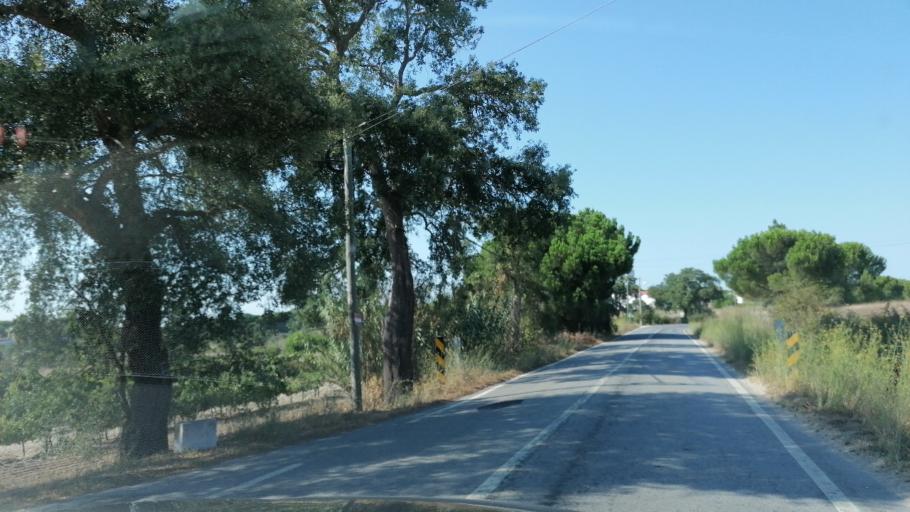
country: PT
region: Santarem
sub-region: Benavente
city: Poceirao
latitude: 38.7598
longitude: -8.6324
